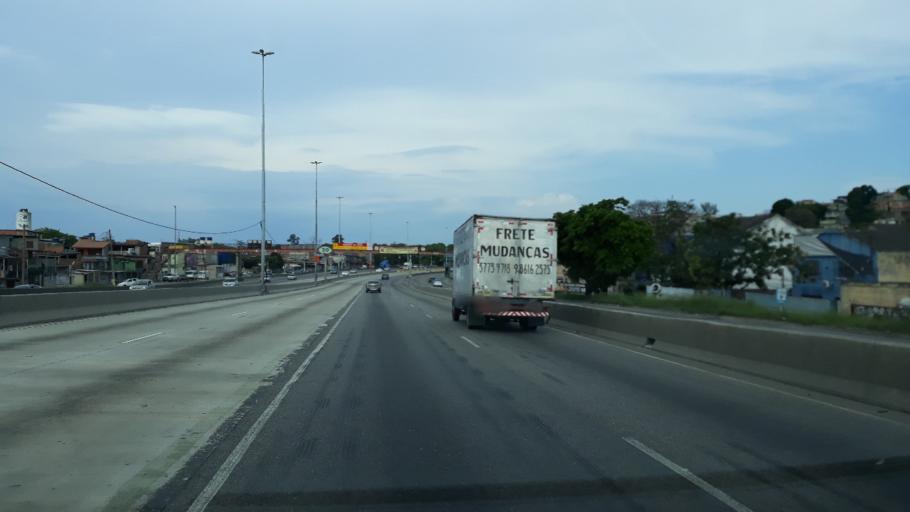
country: BR
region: Rio de Janeiro
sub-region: Duque De Caxias
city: Duque de Caxias
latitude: -22.8149
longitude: -43.2977
